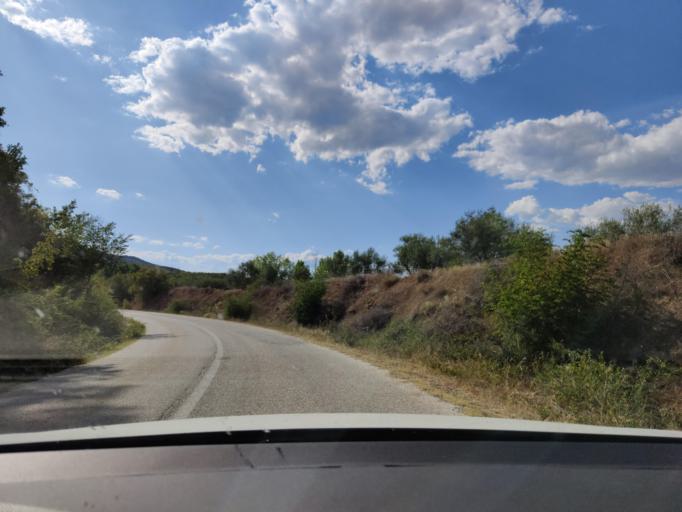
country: GR
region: Central Macedonia
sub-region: Nomos Serron
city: Chrysochorafa
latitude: 41.1475
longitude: 23.2113
